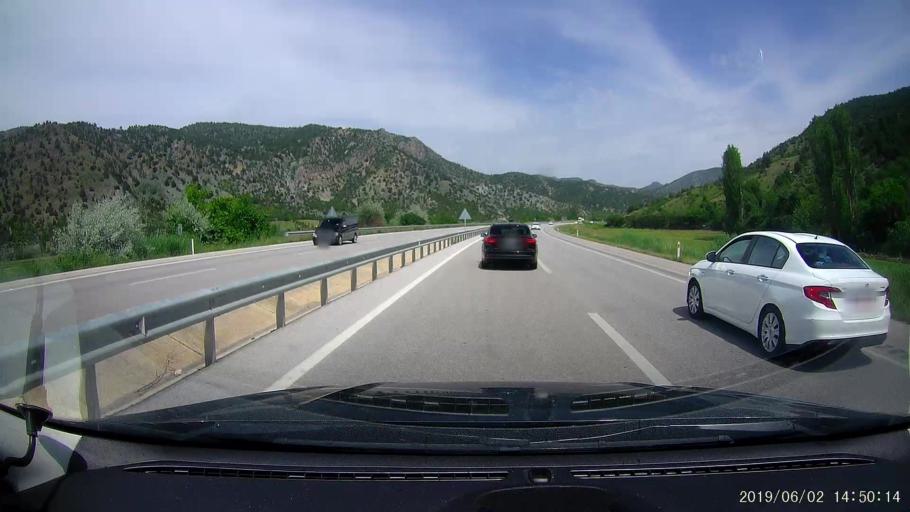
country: TR
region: Corum
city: Hacihamza
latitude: 41.0723
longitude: 34.5141
